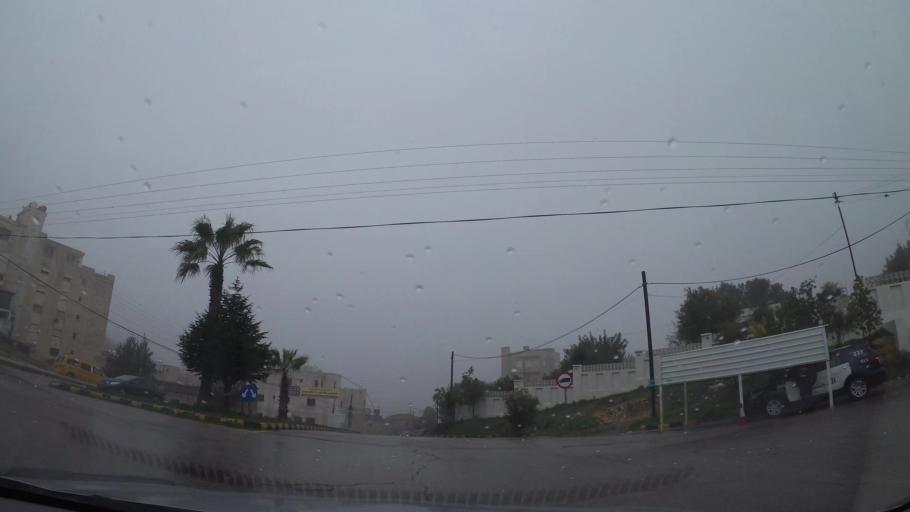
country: JO
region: Amman
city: Al Jubayhah
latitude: 32.0248
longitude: 35.8335
